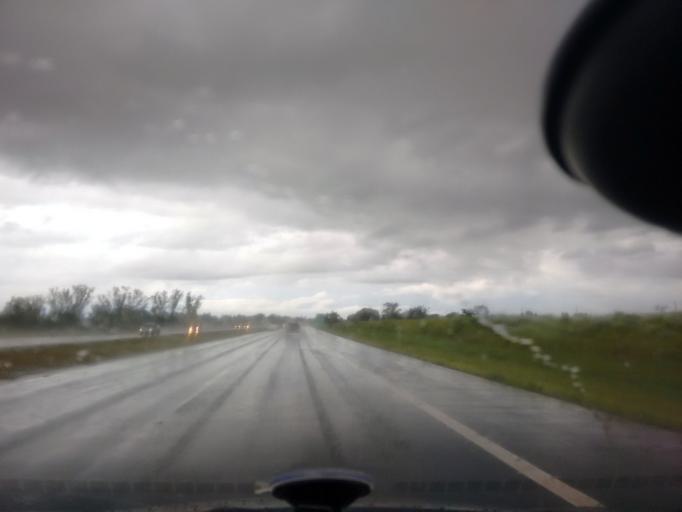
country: BR
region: Sao Paulo
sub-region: Iracemapolis
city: Iracemapolis
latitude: -22.6078
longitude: -47.4594
